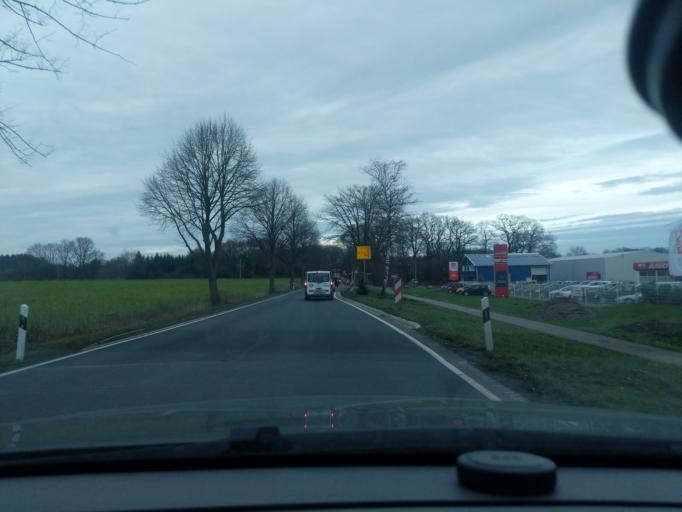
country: DE
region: Lower Saxony
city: Sauensiek
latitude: 53.3761
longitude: 9.5950
